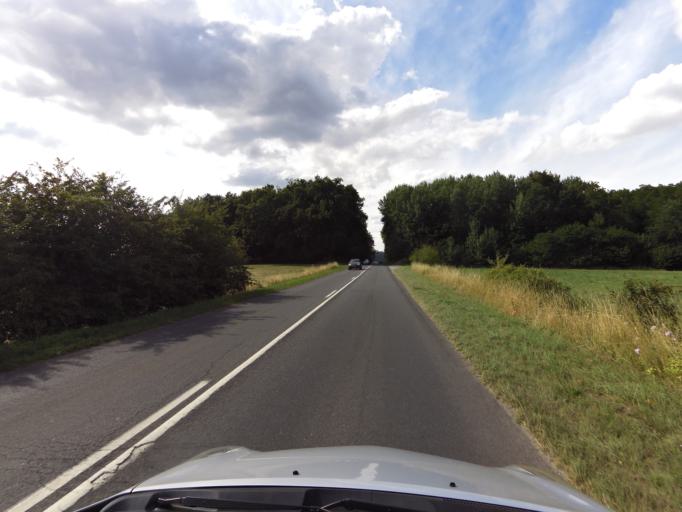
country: FR
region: Picardie
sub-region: Departement de l'Aisne
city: Bruyeres-et-Montberault
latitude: 49.5372
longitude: 3.6454
